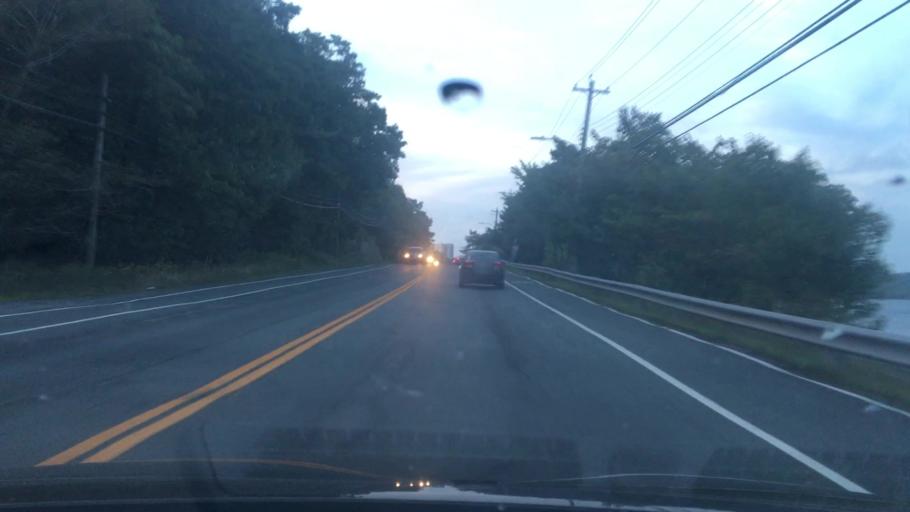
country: CA
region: Nova Scotia
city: Dartmouth
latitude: 44.6896
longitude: -63.6596
